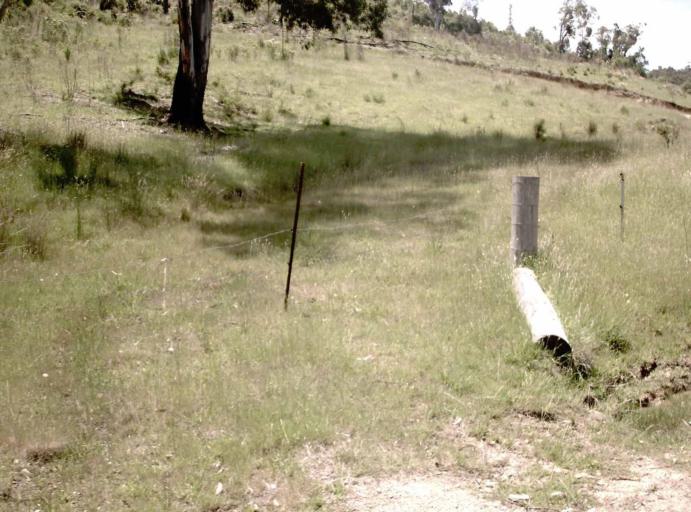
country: AU
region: New South Wales
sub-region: Bombala
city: Bombala
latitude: -37.3613
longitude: 149.0203
